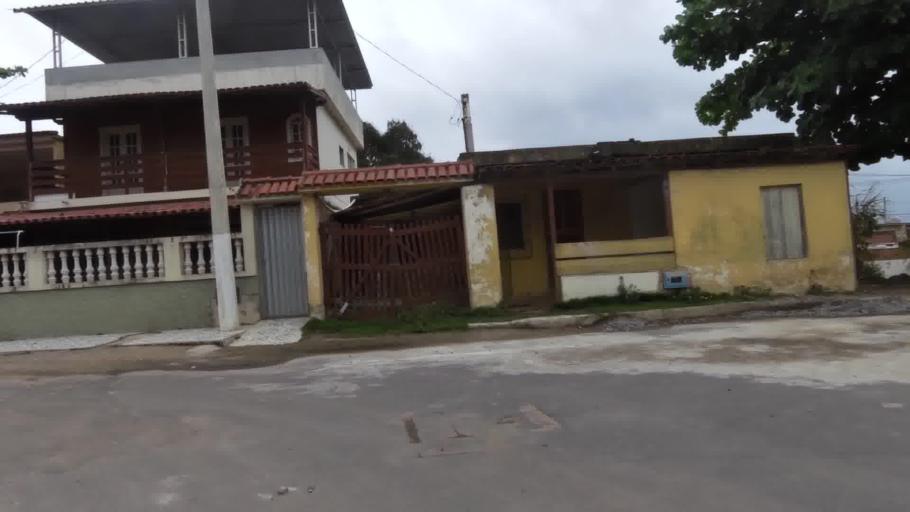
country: BR
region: Espirito Santo
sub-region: Marataizes
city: Marataizes
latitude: -21.0461
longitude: -40.8362
